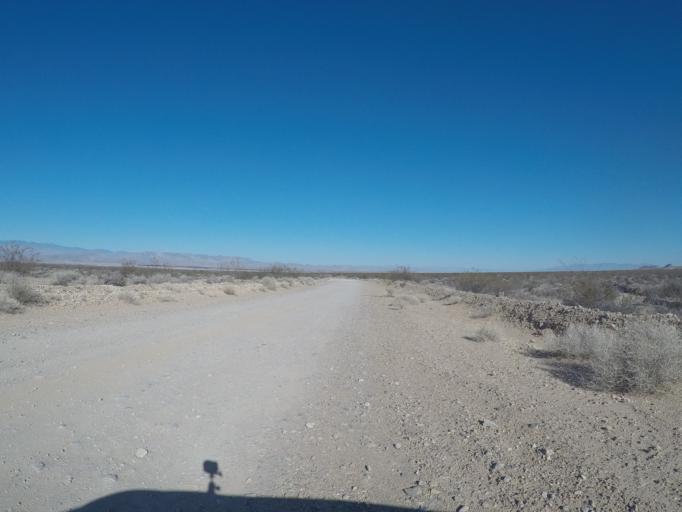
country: US
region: Nevada
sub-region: Clark County
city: Moapa Valley
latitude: 36.4457
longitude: -114.6764
